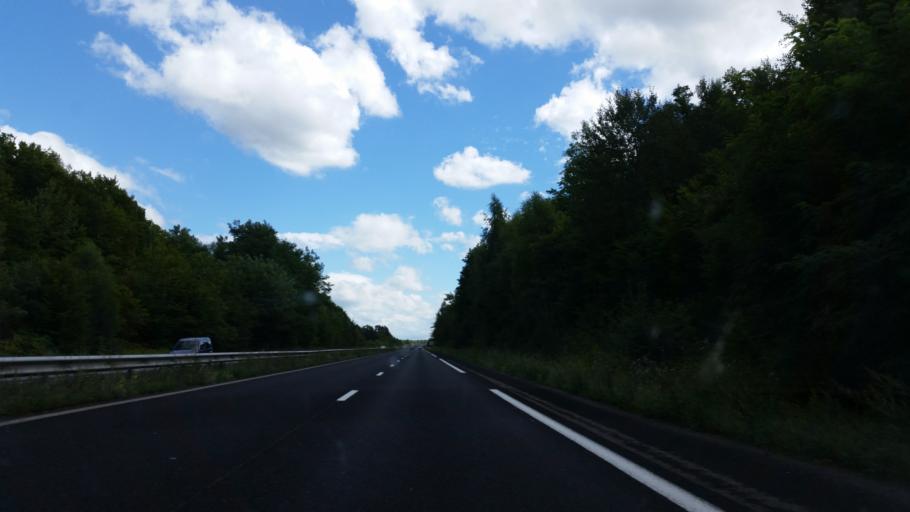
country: FR
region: Lorraine
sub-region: Departement de Meurthe-et-Moselle
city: Bayon
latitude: 48.4905
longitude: 6.2394
